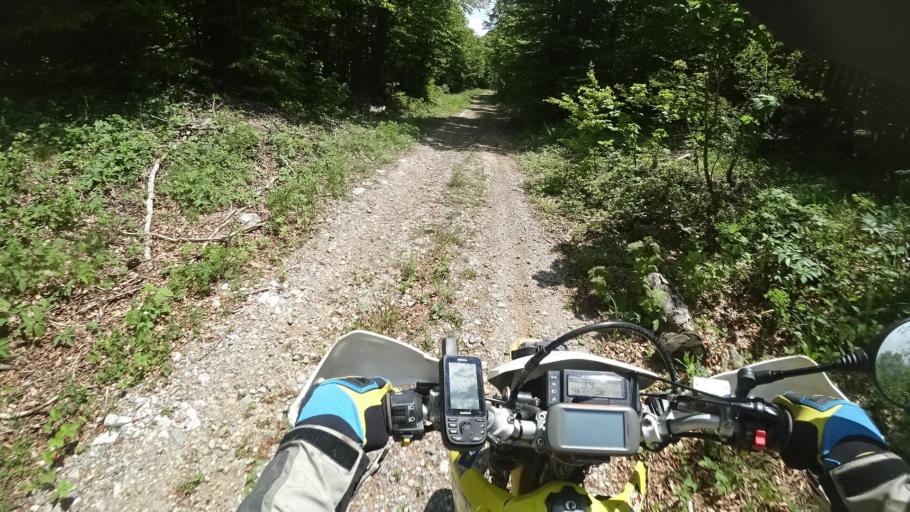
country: HR
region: Zadarska
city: Gracac
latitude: 44.4657
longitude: 15.9022
